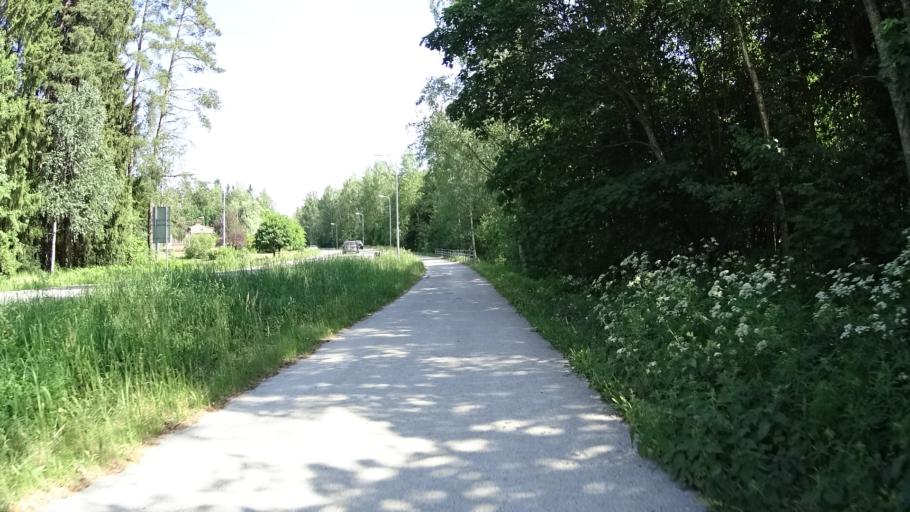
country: FI
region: Uusimaa
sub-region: Raaseporin
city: Karis
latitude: 60.0806
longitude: 23.6648
